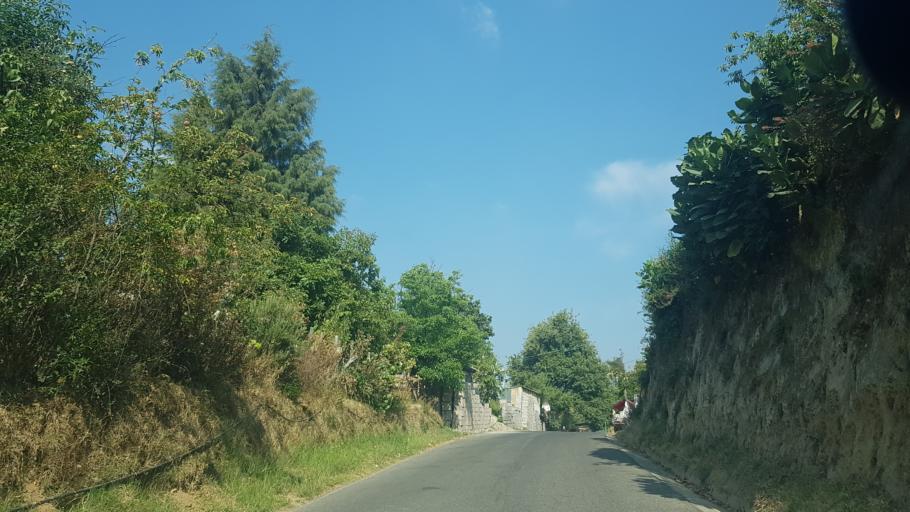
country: MX
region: Puebla
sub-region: Tochimilco
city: Santa Cruz Cuautomatitla
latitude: 18.8946
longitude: -98.6731
